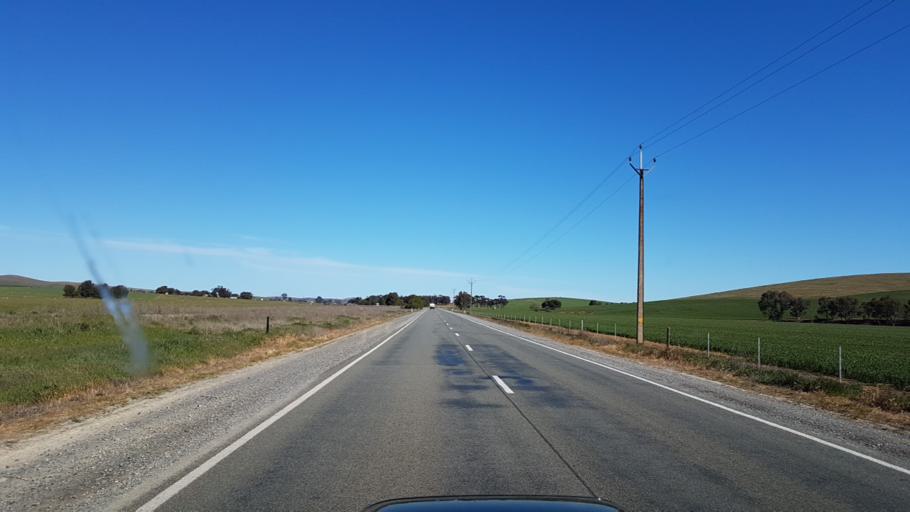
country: AU
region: South Australia
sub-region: Clare and Gilbert Valleys
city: Clare
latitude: -33.6069
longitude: 138.8925
